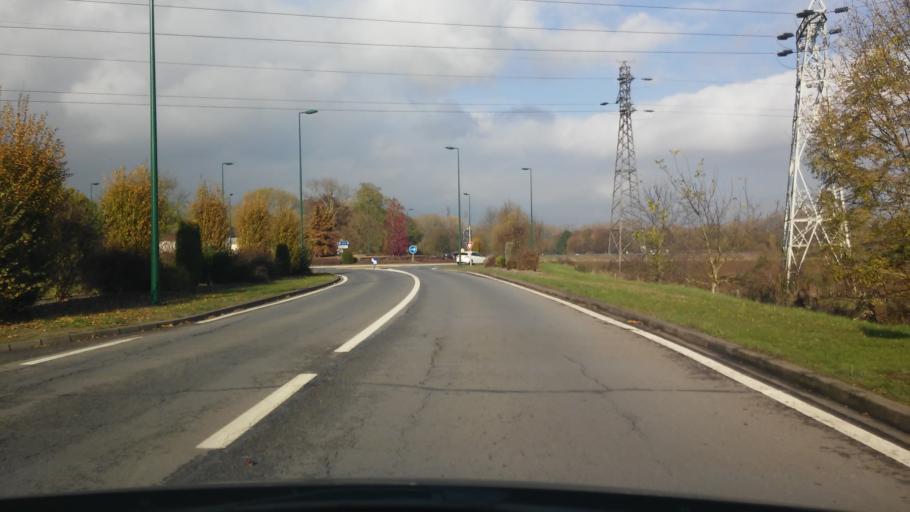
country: FR
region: Lorraine
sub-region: Departement de la Moselle
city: Richemont
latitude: 49.2829
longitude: 6.1694
